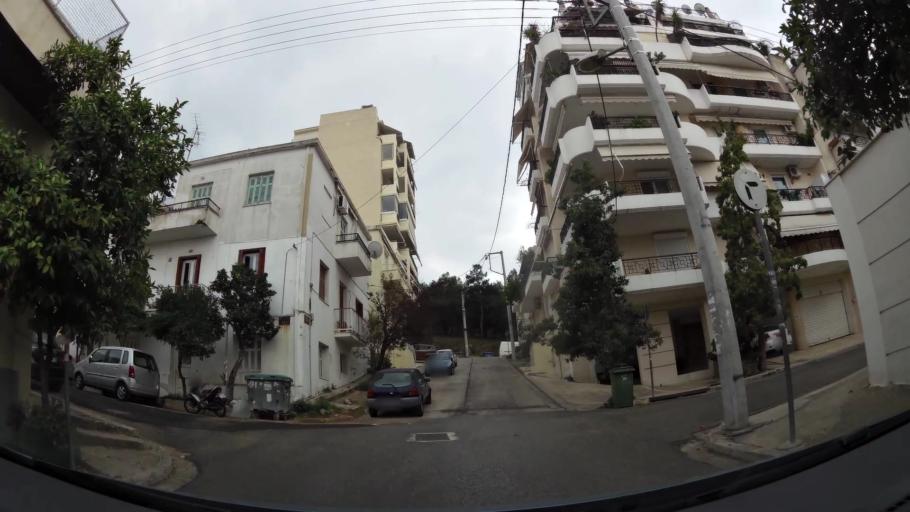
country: GR
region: Attica
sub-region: Nomarchia Athinas
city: Kaisariani
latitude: 37.9646
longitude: 23.7674
